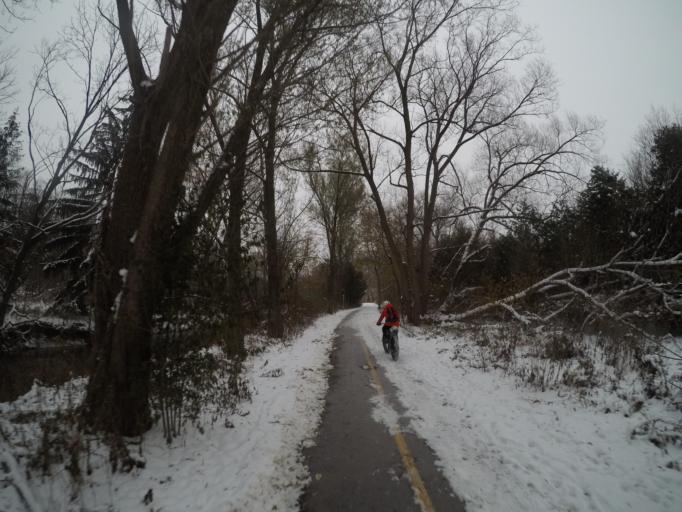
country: CA
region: Ontario
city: Waterloo
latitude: 43.4841
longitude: -80.5149
